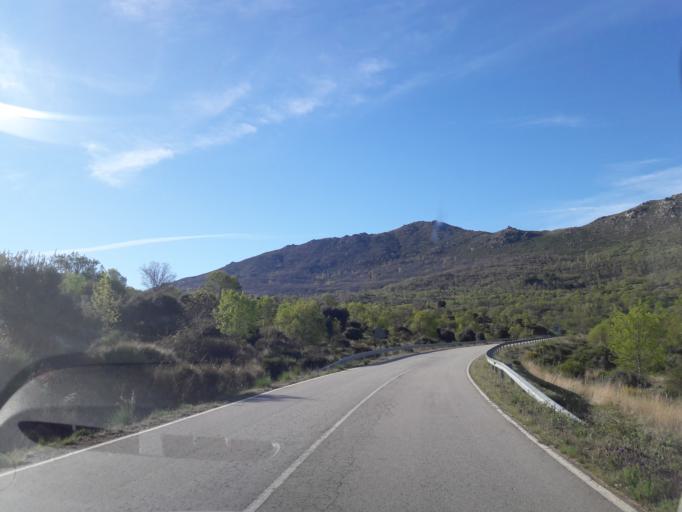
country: ES
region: Castille and Leon
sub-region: Provincia de Salamanca
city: Sanchotello
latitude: 40.4473
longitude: -5.7362
